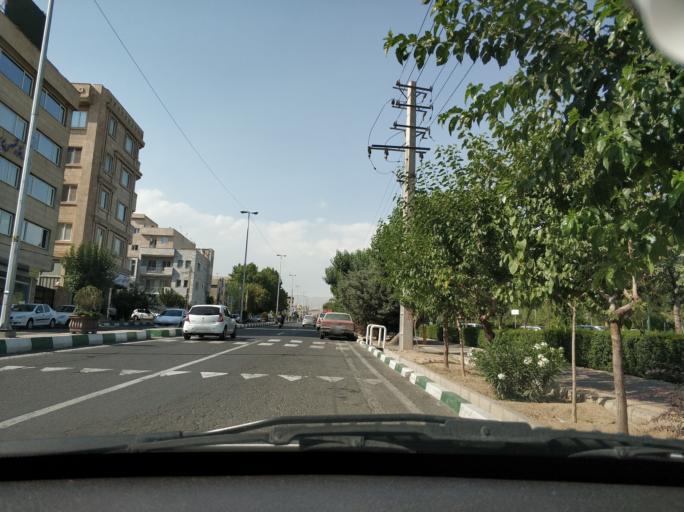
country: IR
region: Tehran
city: Tajrish
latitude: 35.7544
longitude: 51.5387
